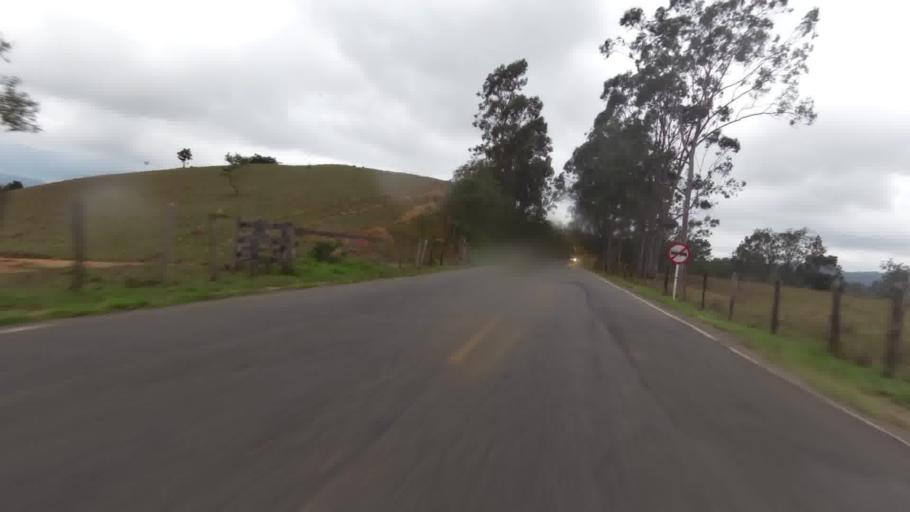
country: BR
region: Espirito Santo
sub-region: Alfredo Chaves
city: Alfredo Chaves
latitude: -20.6685
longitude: -40.7355
